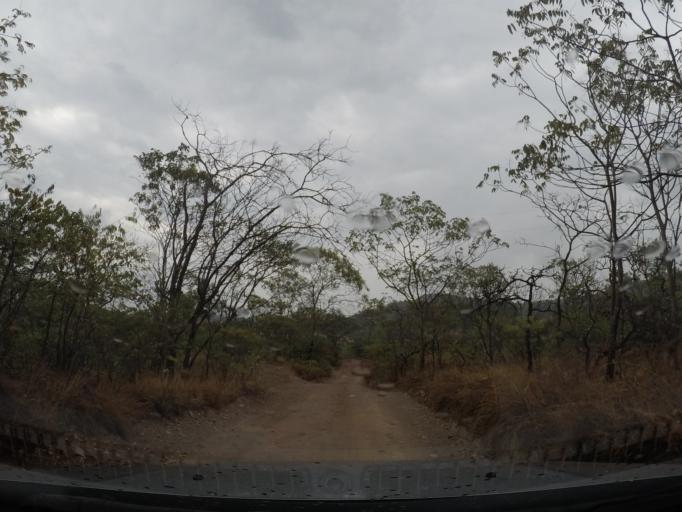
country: BR
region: Goias
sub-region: Pirenopolis
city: Pirenopolis
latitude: -15.8224
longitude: -48.8881
